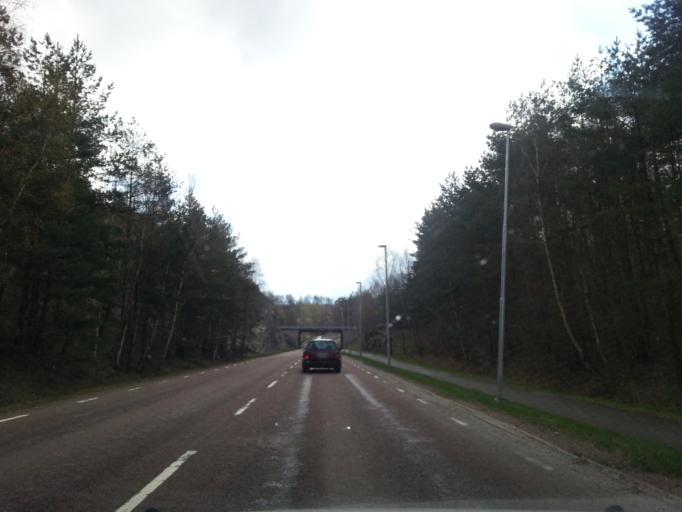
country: SE
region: Vaestra Goetaland
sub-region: Goteborg
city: Hammarkullen
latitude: 57.7890
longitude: 12.0331
